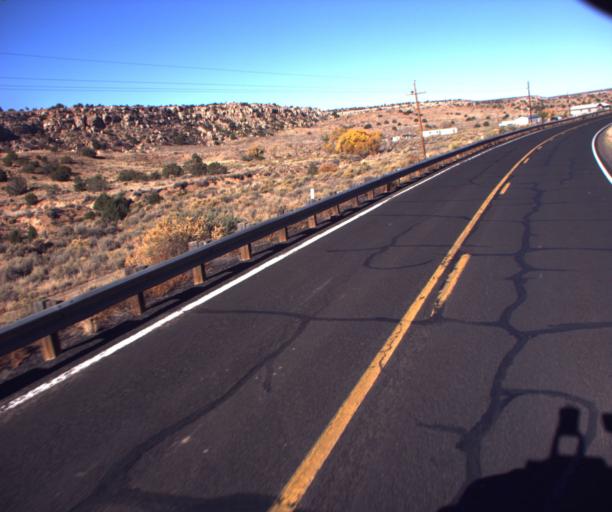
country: US
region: Arizona
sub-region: Navajo County
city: First Mesa
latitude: 35.8173
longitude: -110.2152
